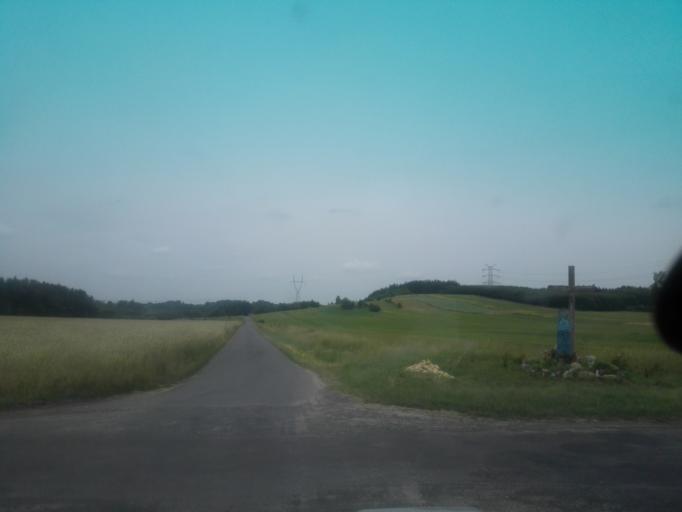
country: PL
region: Silesian Voivodeship
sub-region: Powiat czestochowski
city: Mstow
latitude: 50.8280
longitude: 19.3295
